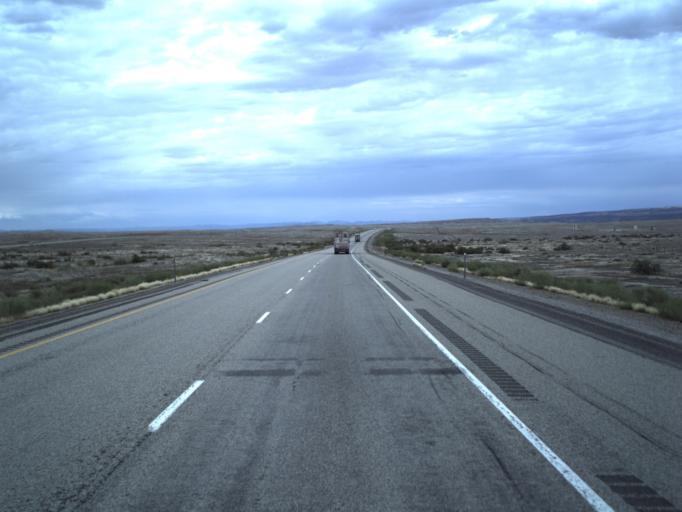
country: US
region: Utah
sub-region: Grand County
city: Moab
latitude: 38.9643
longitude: -109.3728
